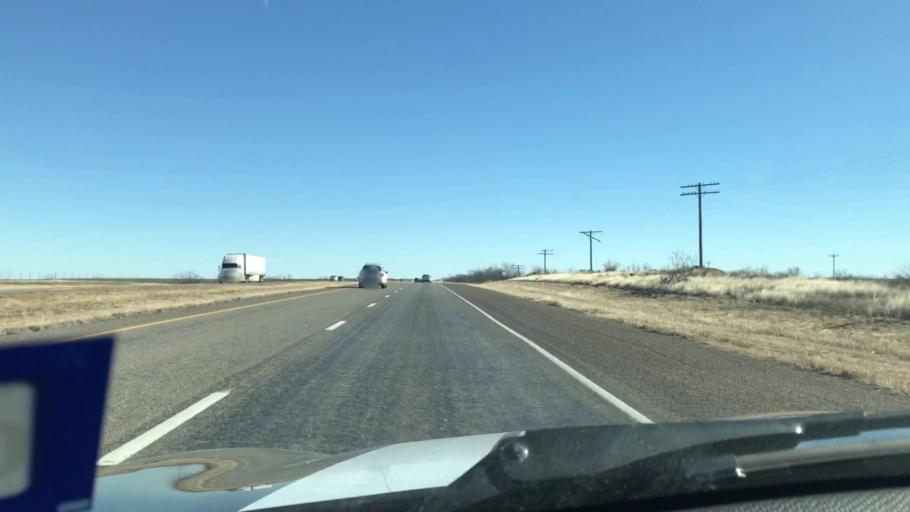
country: US
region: Texas
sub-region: Garza County
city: Post
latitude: 33.1307
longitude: -101.3001
